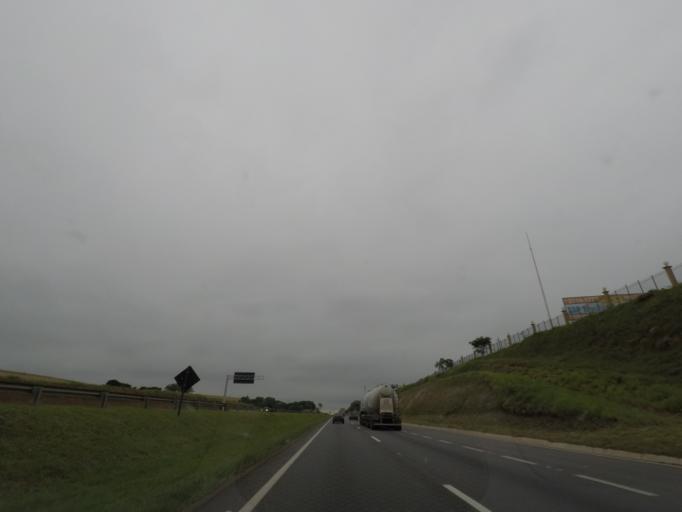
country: BR
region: Sao Paulo
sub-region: Jarinu
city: Jarinu
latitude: -23.0374
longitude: -46.7005
